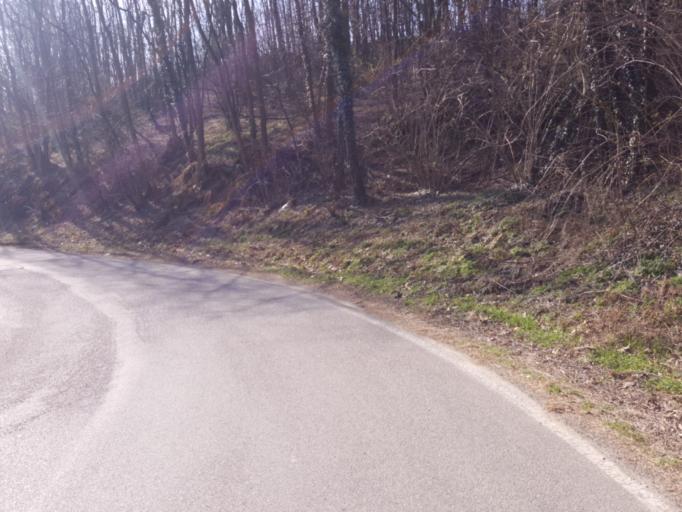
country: IT
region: Lombardy
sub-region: Provincia di Como
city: Novedrate
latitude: 45.6912
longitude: 9.1104
